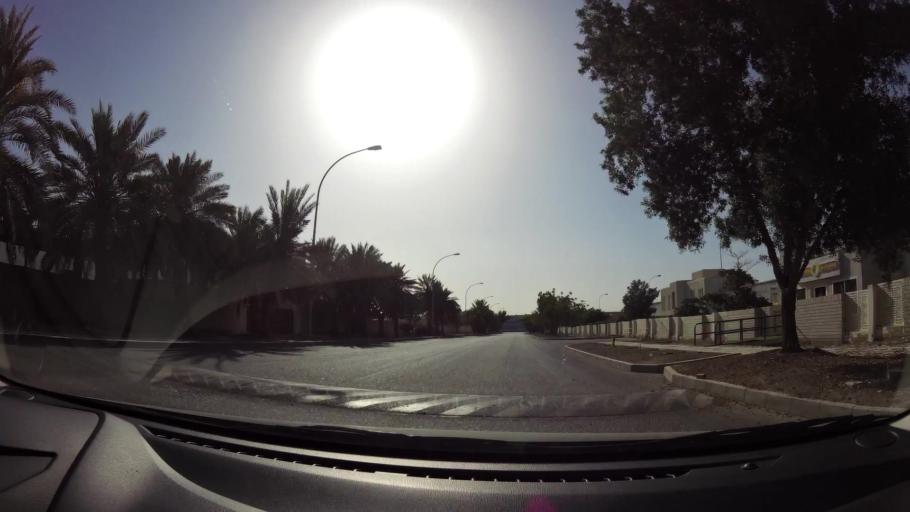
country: OM
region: Muhafazat Masqat
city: As Sib al Jadidah
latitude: 23.5535
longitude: 58.2160
